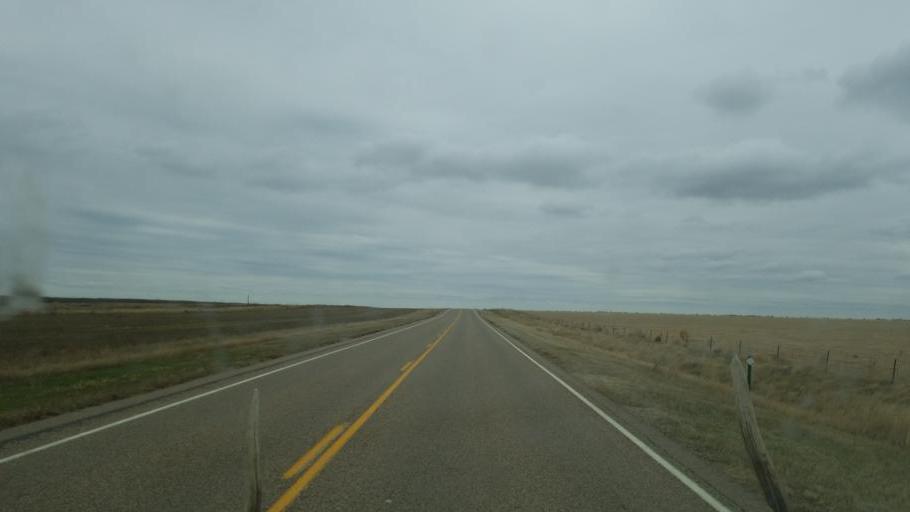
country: US
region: Colorado
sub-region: Cheyenne County
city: Cheyenne Wells
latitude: 38.8491
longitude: -102.2380
